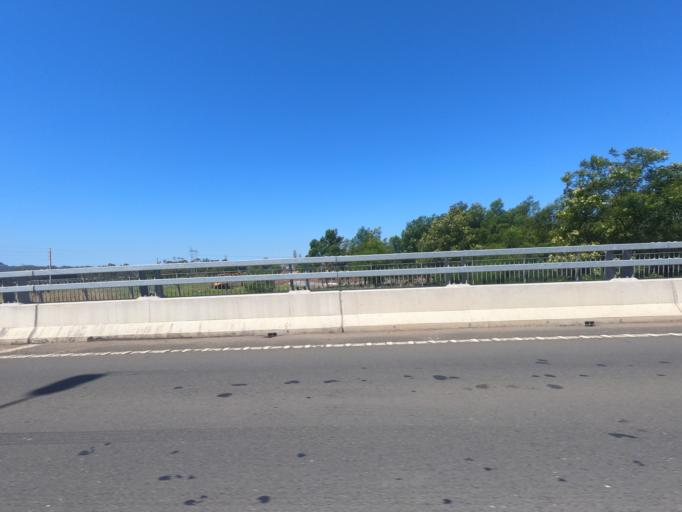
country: AU
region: New South Wales
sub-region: Wollongong
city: Dapto
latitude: -34.4799
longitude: 150.7657
